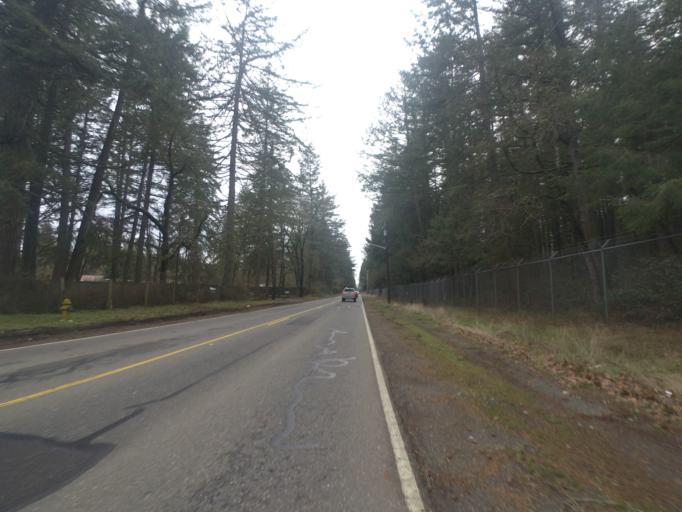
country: US
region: Washington
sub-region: Pierce County
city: McChord Air Force Base
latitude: 47.1217
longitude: -122.5147
